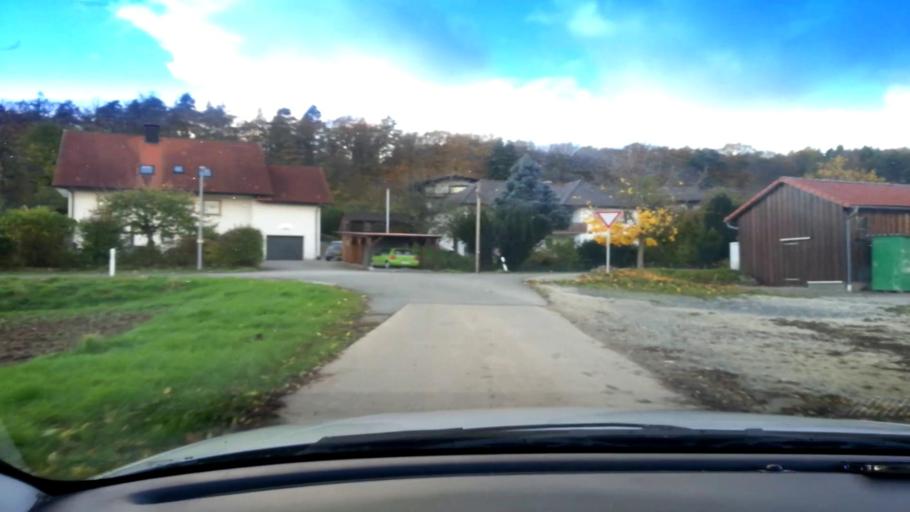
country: DE
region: Bavaria
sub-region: Upper Franconia
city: Zapfendorf
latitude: 50.0483
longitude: 10.9261
